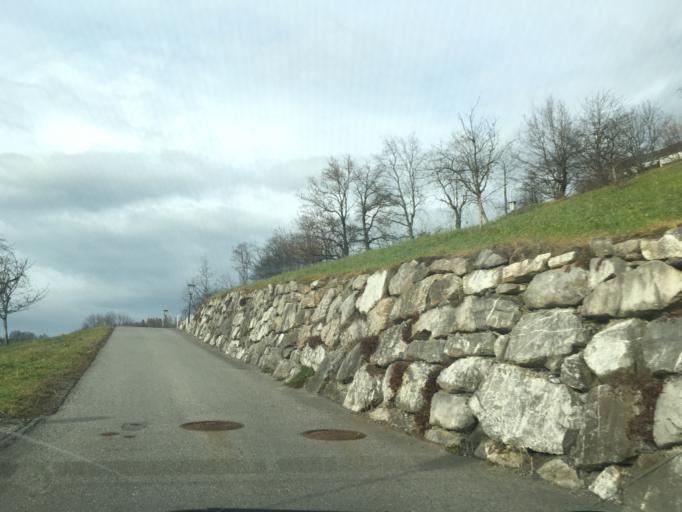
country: AT
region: Vorarlberg
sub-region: Politischer Bezirk Feldkirch
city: Klaus
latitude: 47.3113
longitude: 9.6437
